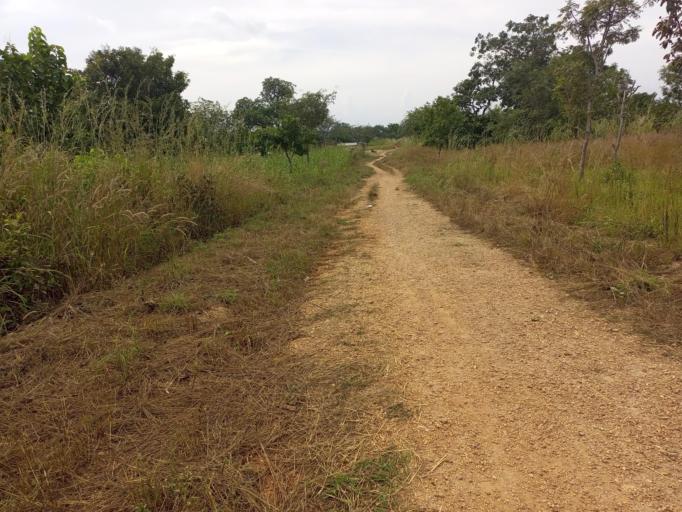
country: TG
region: Kara
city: Niamtougou
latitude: 9.8247
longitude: 0.9974
